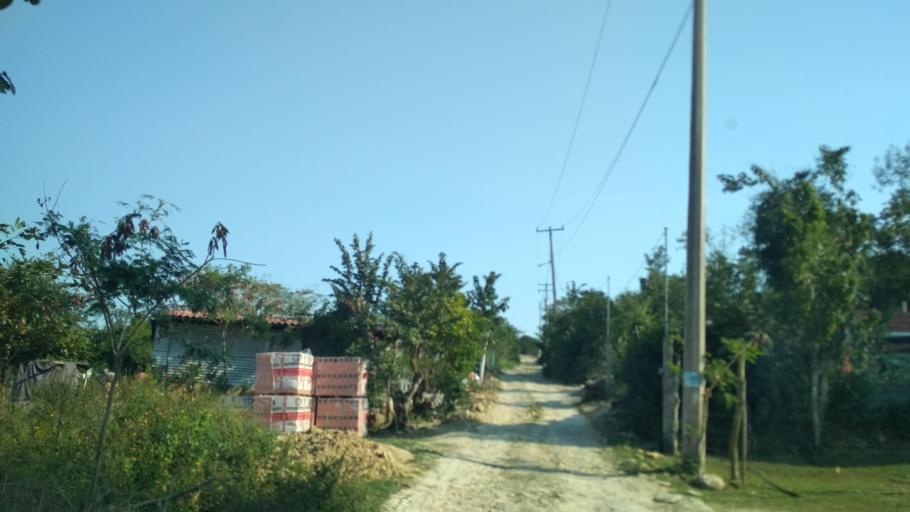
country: MM
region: Shan
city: Taunggyi
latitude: 20.4008
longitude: 97.3272
